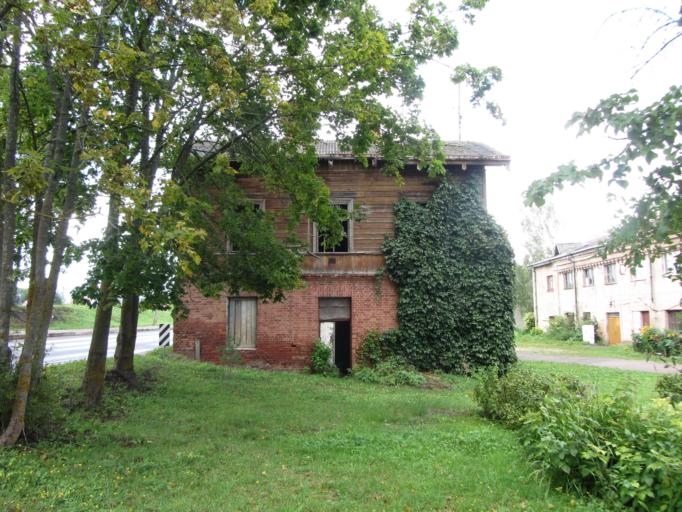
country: LT
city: Dukstas
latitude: 55.5200
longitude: 26.3246
